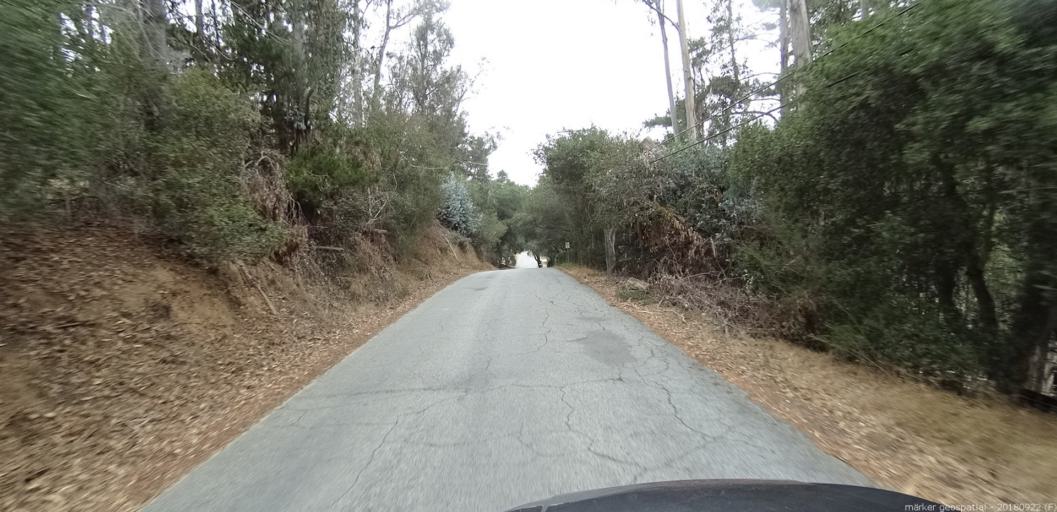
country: US
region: California
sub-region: Monterey County
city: Prunedale
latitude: 36.7900
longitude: -121.6748
